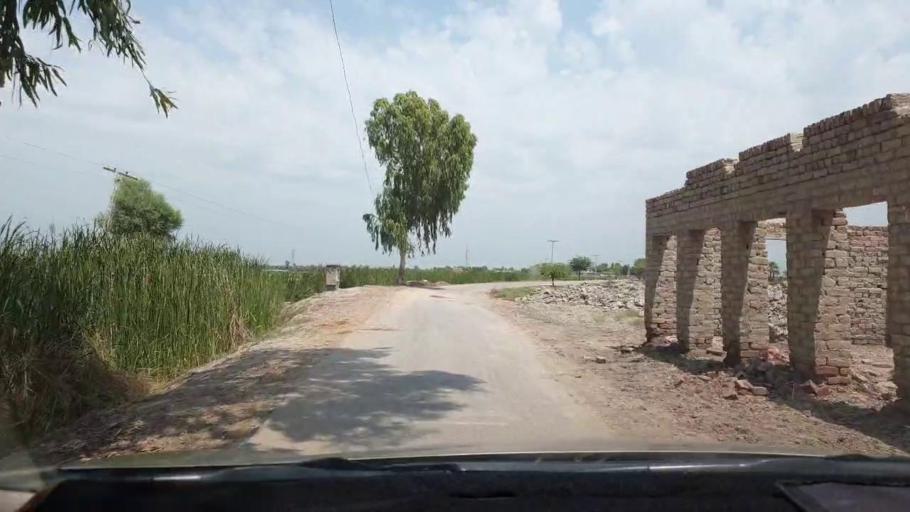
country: PK
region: Sindh
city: Naudero
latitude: 27.7224
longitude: 68.3315
